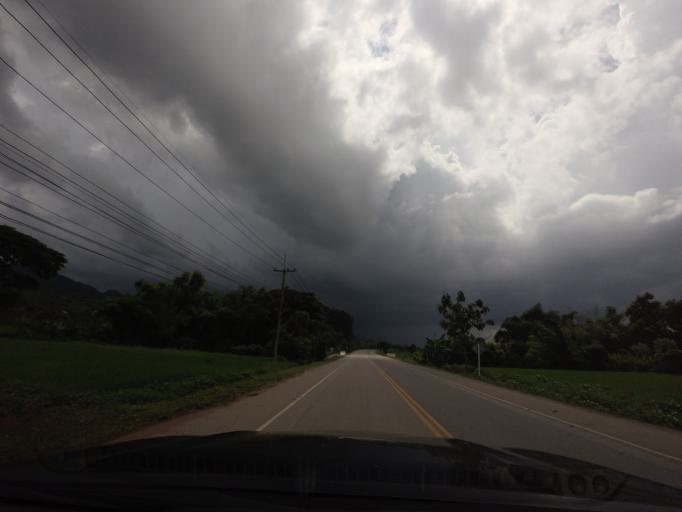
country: LA
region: Vientiane
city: Muang Sanakham
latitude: 17.9850
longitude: 101.7481
